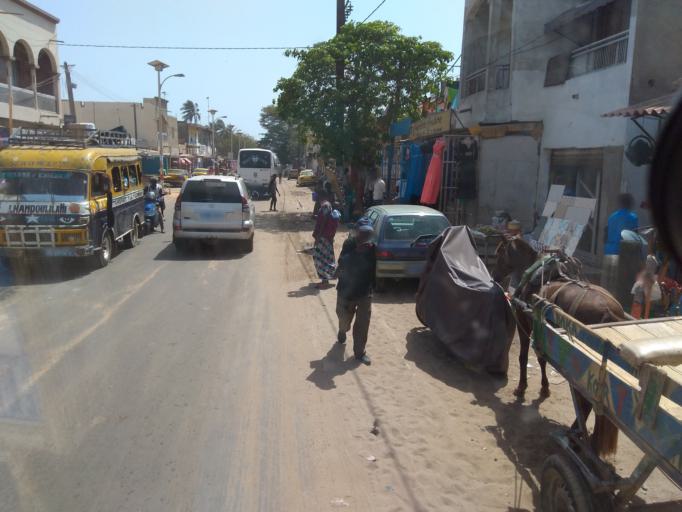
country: SN
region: Dakar
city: Pikine
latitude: 14.7635
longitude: -17.3744
